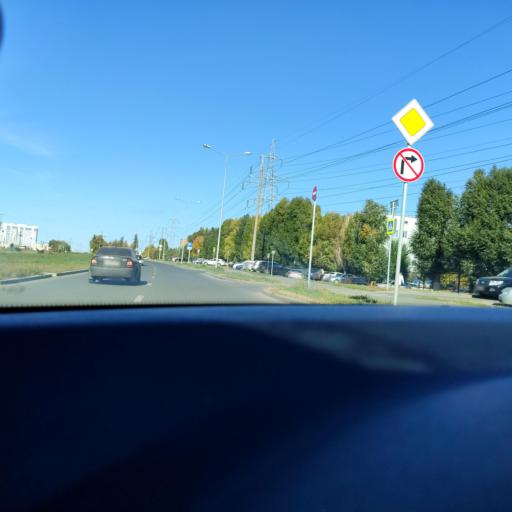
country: RU
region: Samara
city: Samara
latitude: 53.2562
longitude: 50.2461
